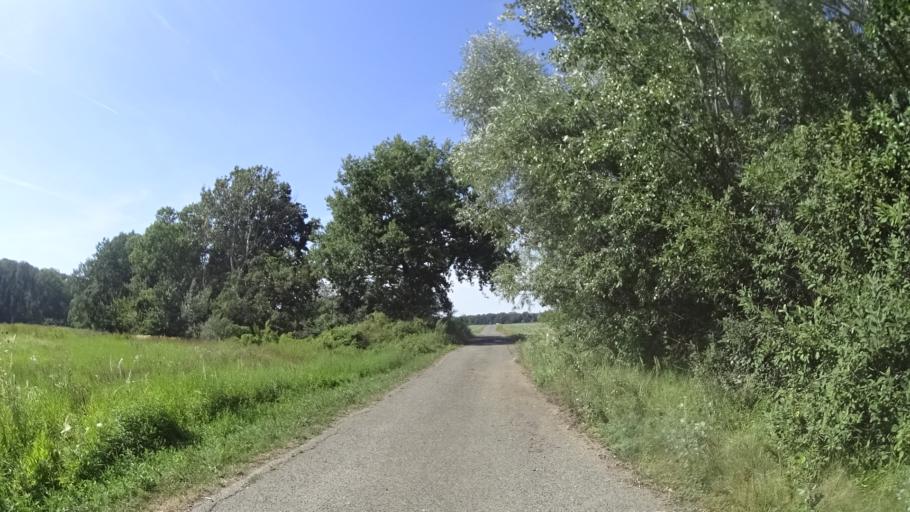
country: AT
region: Lower Austria
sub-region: Politischer Bezirk Ganserndorf
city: Angern an der March
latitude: 48.3624
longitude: 16.8720
